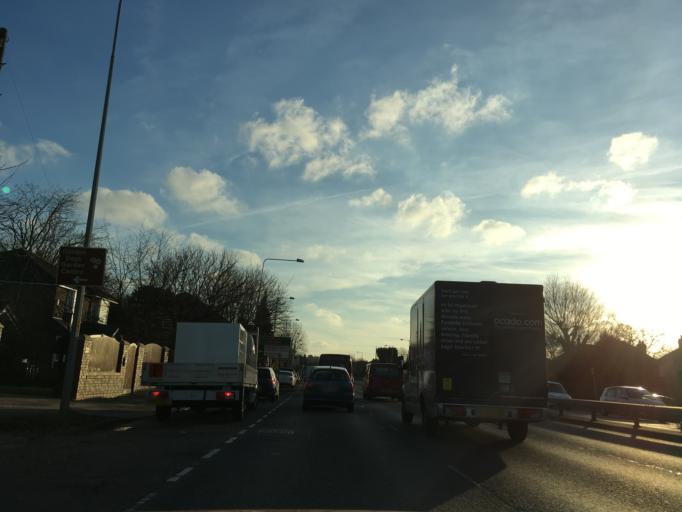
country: GB
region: England
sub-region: Manchester
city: Didsbury
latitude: 53.3938
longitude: -2.2265
